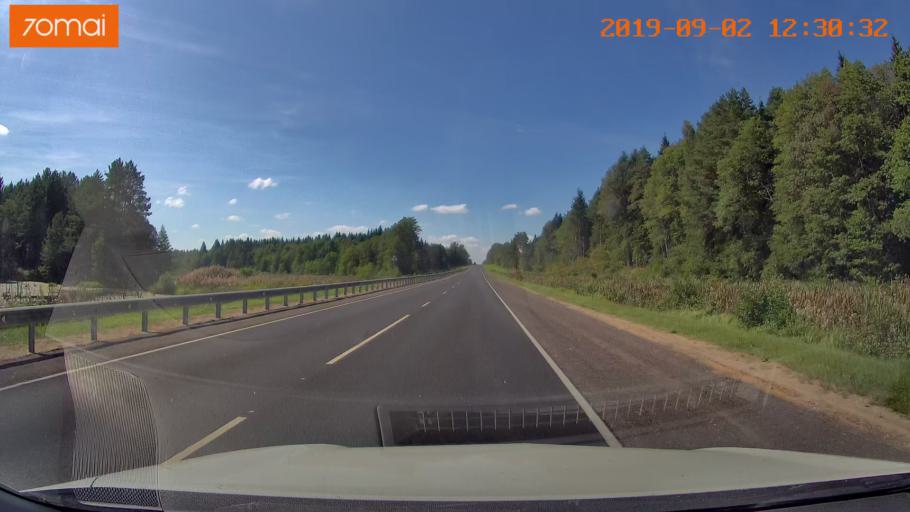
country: RU
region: Smolensk
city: Shumyachi
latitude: 53.8313
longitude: 32.4720
